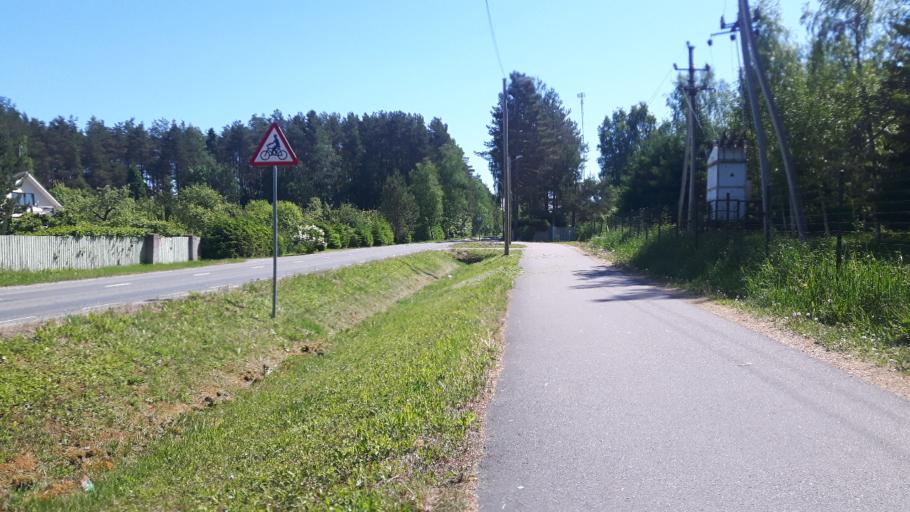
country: EE
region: Harju
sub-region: Saku vald
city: Saku
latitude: 59.2190
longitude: 24.6740
